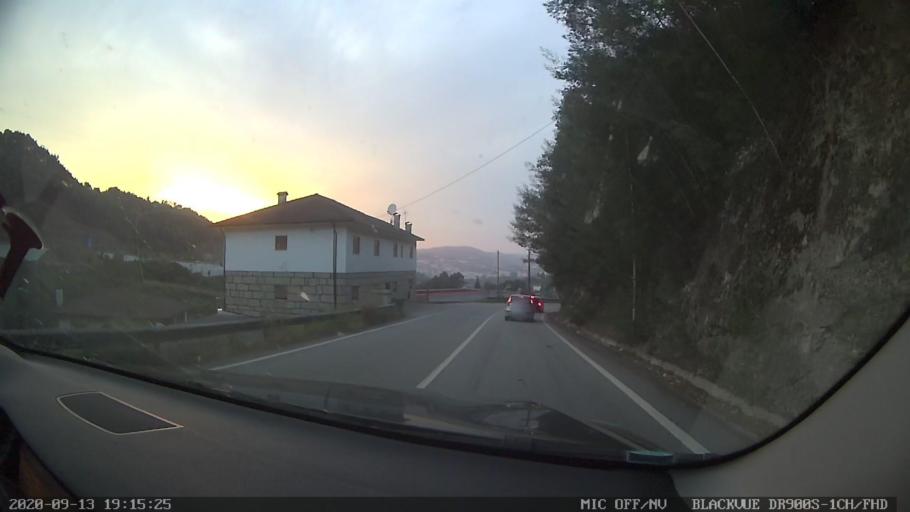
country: PT
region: Porto
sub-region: Amarante
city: Amarante
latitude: 41.2611
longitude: -8.0598
